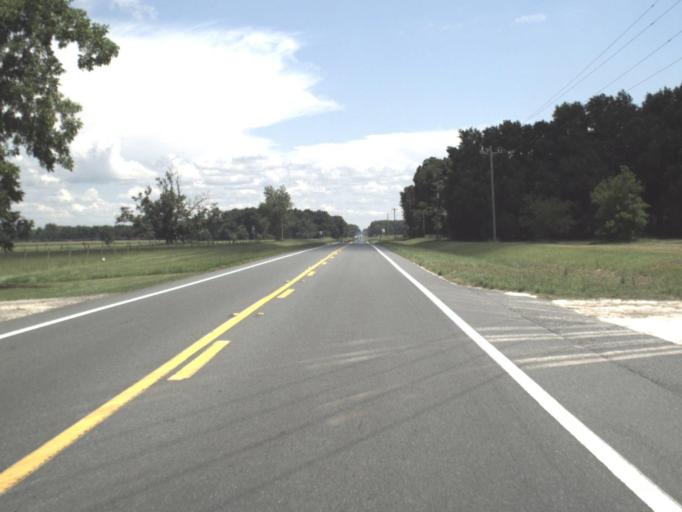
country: US
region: Florida
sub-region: Lafayette County
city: Mayo
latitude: 30.1125
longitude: -83.2548
